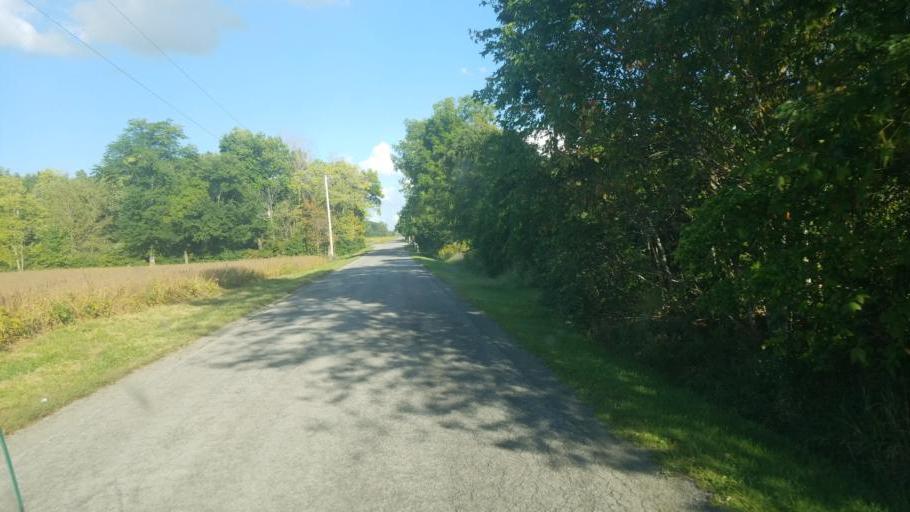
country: US
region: Ohio
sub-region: Hancock County
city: Arlington
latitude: 40.9359
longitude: -83.6722
